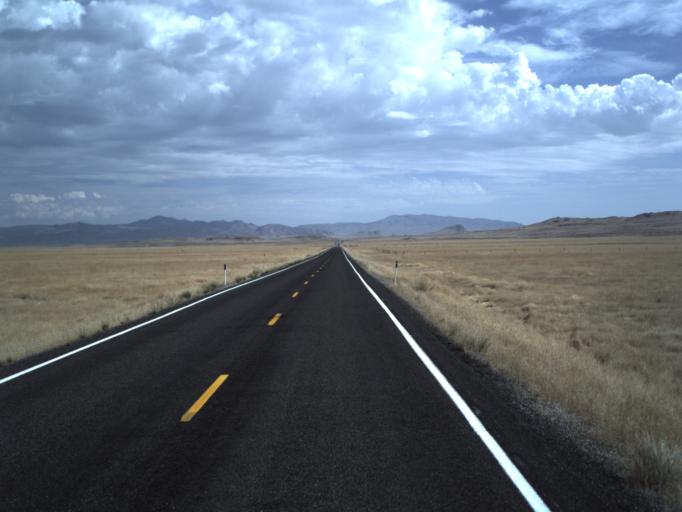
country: US
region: Utah
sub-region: Tooele County
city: Wendover
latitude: 41.3892
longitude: -113.9761
